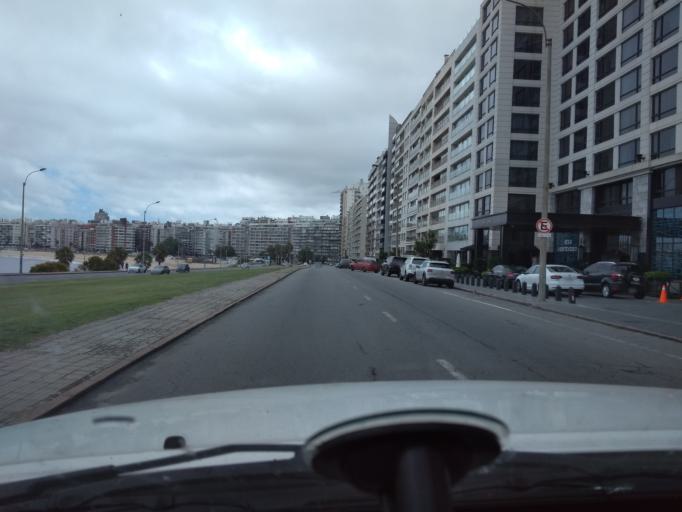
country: UY
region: Montevideo
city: Montevideo
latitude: -34.9101
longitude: -56.1381
